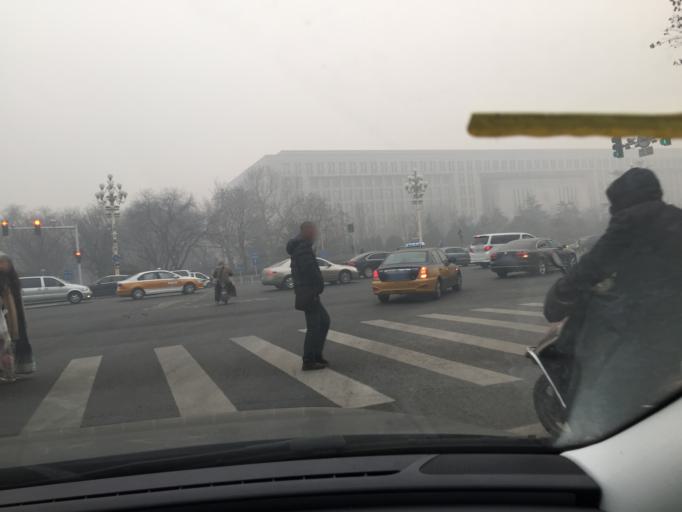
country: CN
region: Beijing
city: Beijing
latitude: 39.9070
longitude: 116.4004
